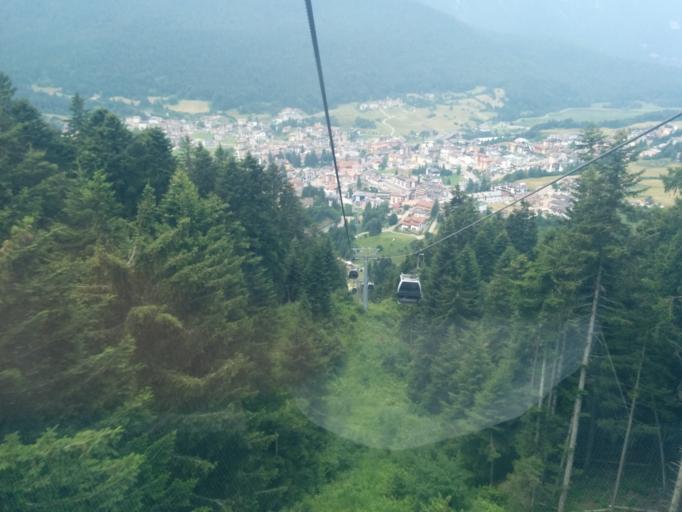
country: IT
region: Trentino-Alto Adige
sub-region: Provincia di Trento
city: Andalo
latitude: 46.1574
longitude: 11.0110
